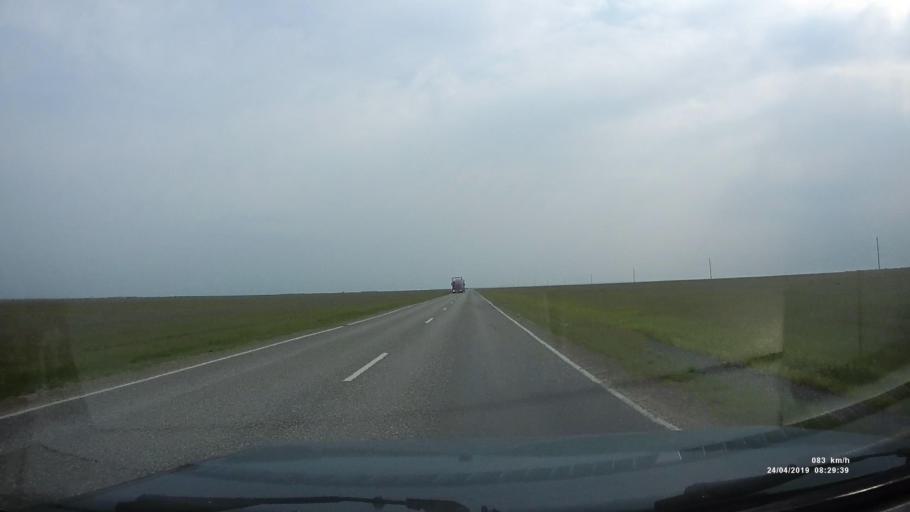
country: RU
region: Kalmykiya
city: Priyutnoye
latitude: 46.1537
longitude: 43.8339
